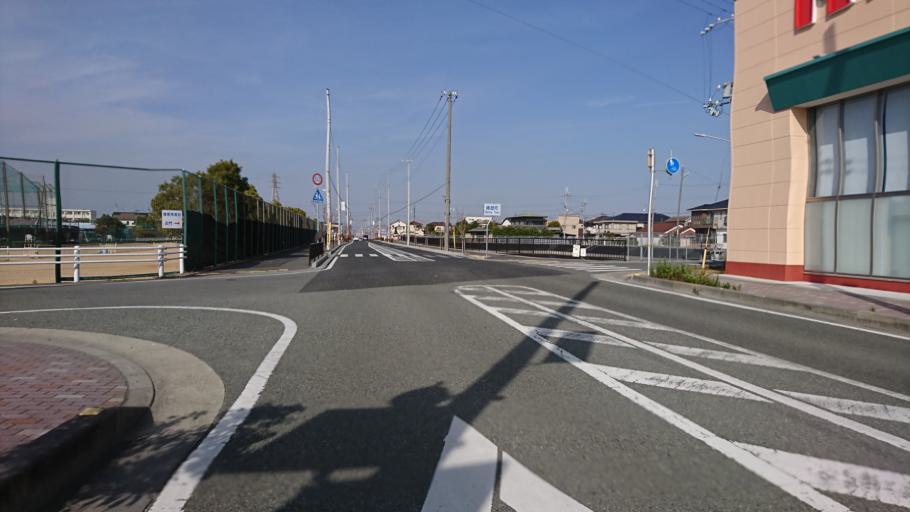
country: JP
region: Hyogo
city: Kakogawacho-honmachi
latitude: 34.7067
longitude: 134.8744
